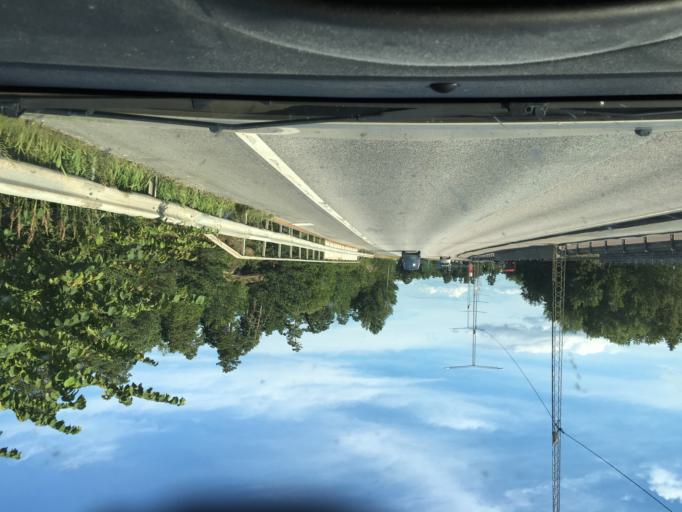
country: SE
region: Stockholm
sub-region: Nacka Kommun
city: Boo
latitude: 59.3198
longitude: 18.2569
